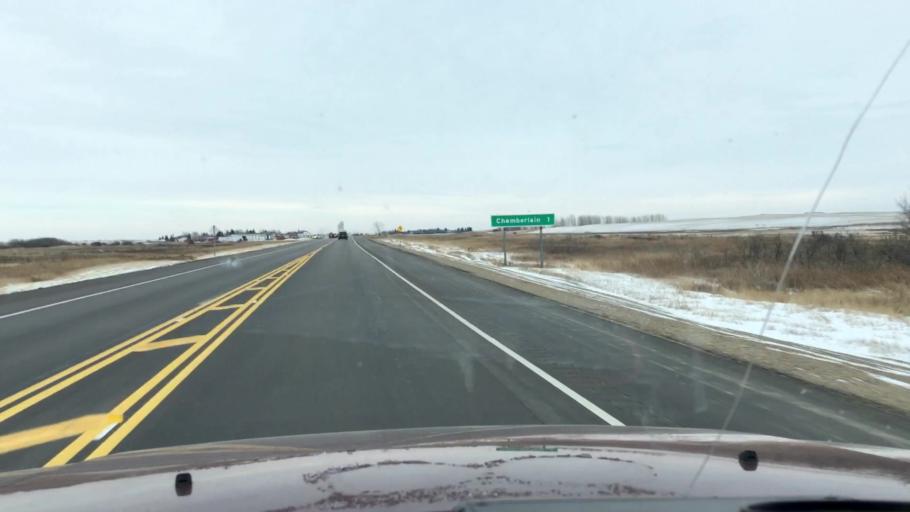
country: CA
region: Saskatchewan
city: Moose Jaw
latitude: 50.8597
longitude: -105.5858
